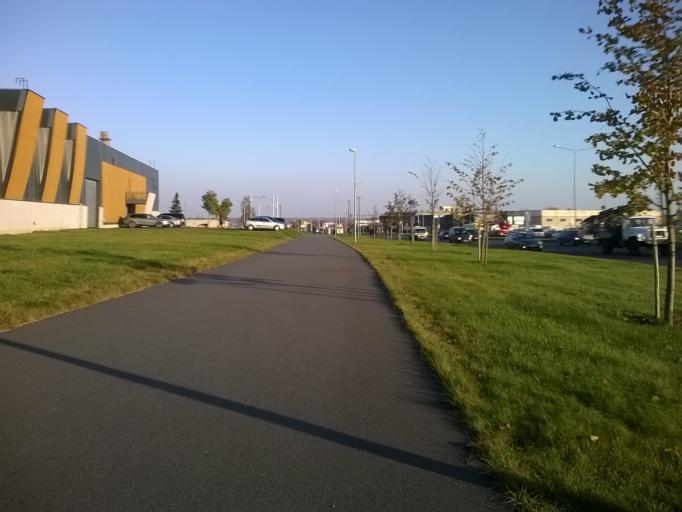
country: EE
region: Tartu
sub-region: UElenurme vald
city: Ulenurme
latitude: 58.3434
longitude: 26.7223
